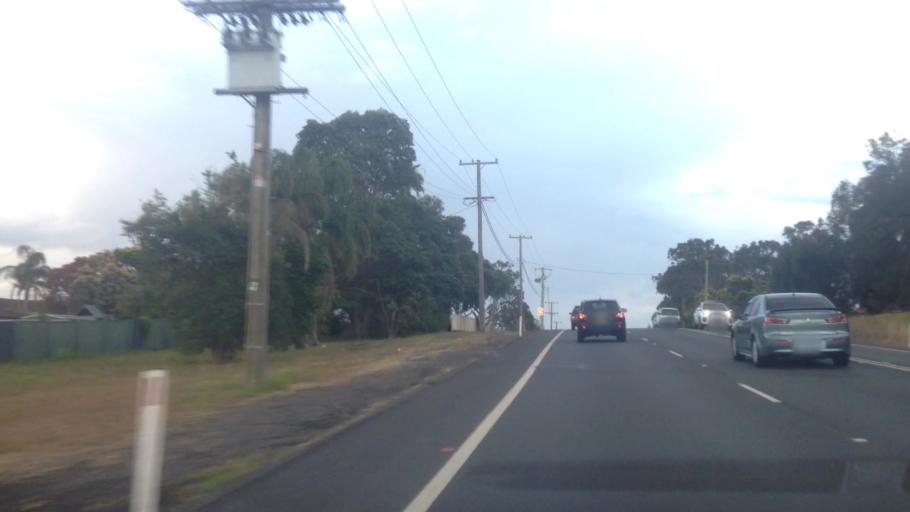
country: AU
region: New South Wales
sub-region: Wyong Shire
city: Kanwal
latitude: -33.2602
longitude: 151.4845
